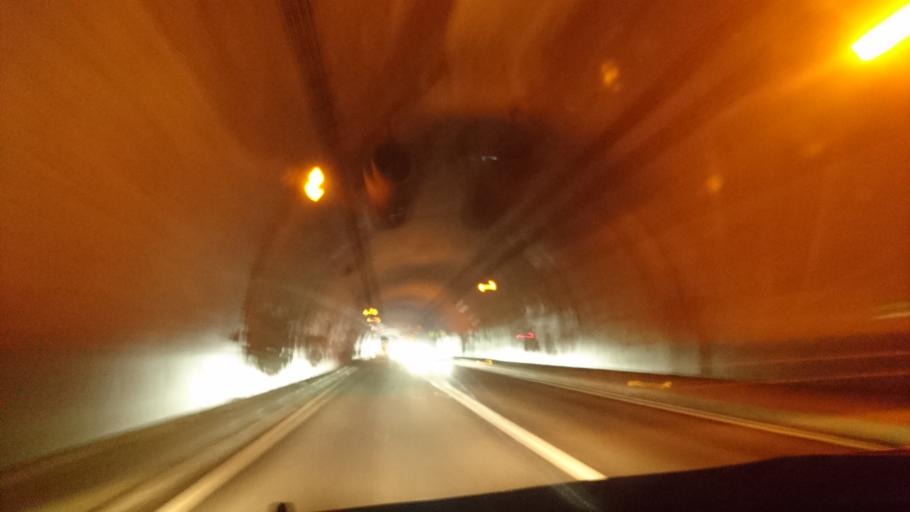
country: JP
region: Iwate
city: Ichinoseki
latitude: 38.9782
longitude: 141.2275
